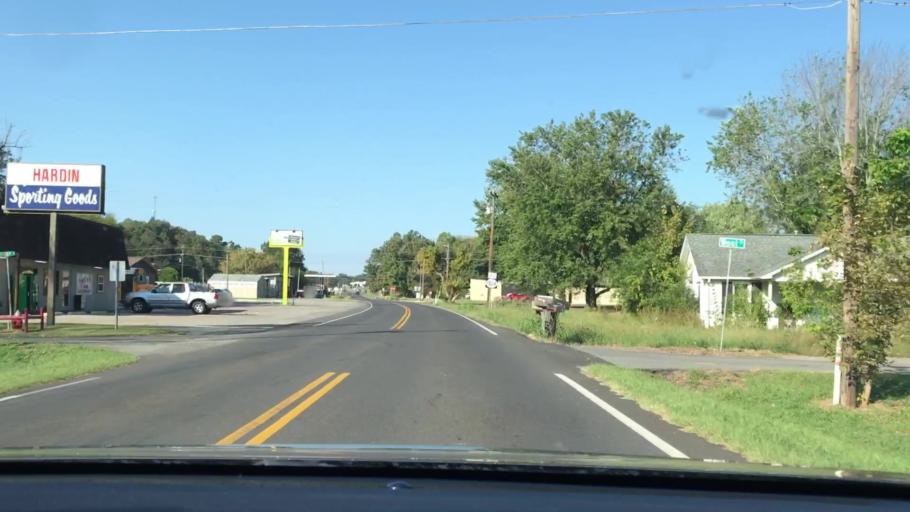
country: US
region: Kentucky
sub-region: Marshall County
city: Benton
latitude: 36.7671
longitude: -88.3016
